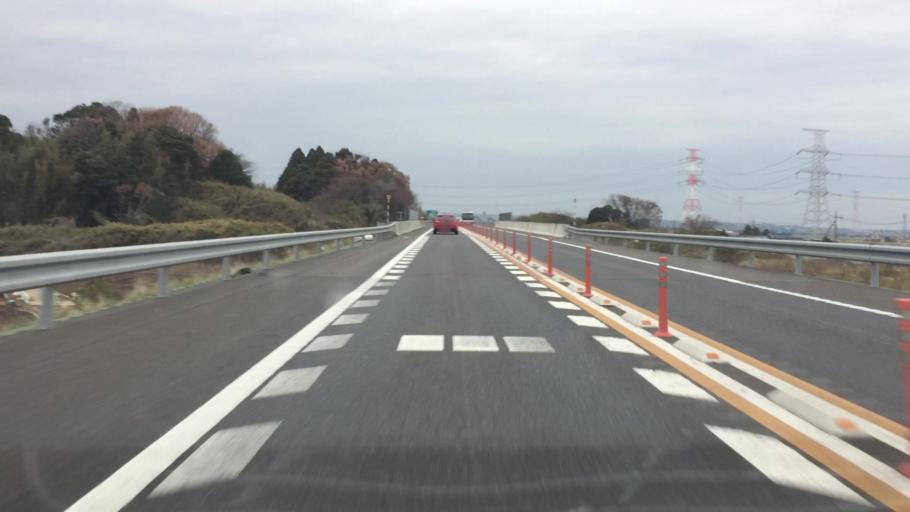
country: JP
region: Ibaraki
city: Edosaki
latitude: 35.8812
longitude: 140.3849
